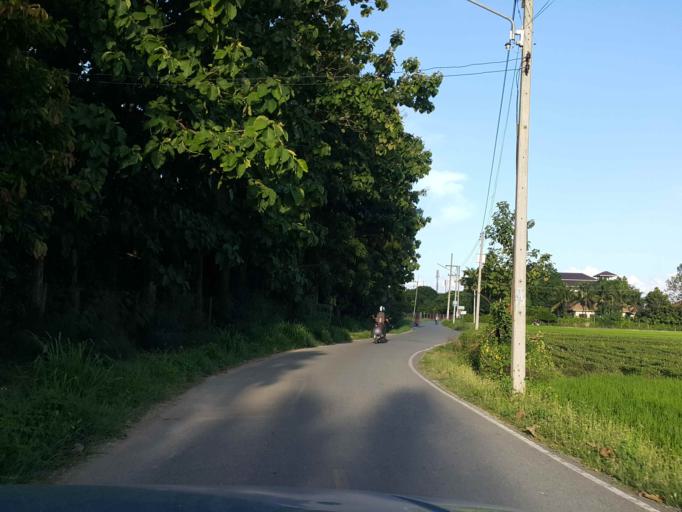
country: TH
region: Chiang Mai
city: San Sai
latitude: 18.8962
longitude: 98.9963
